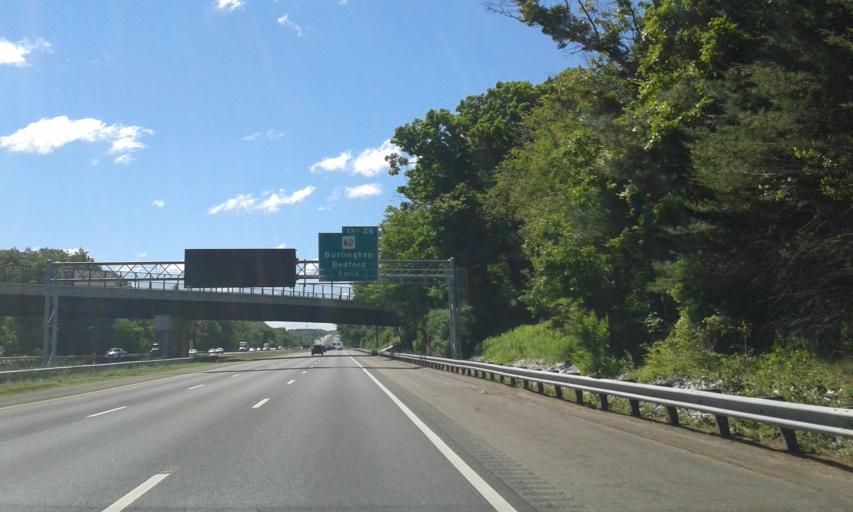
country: US
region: Massachusetts
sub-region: Middlesex County
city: Bedford
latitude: 42.5186
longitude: -71.2601
